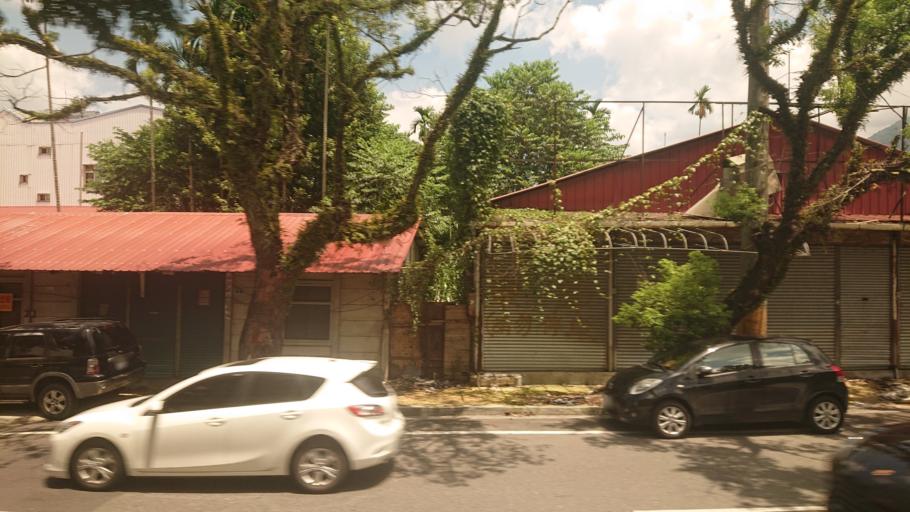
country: TW
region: Taiwan
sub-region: Nantou
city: Puli
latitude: 23.9742
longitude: 120.9794
